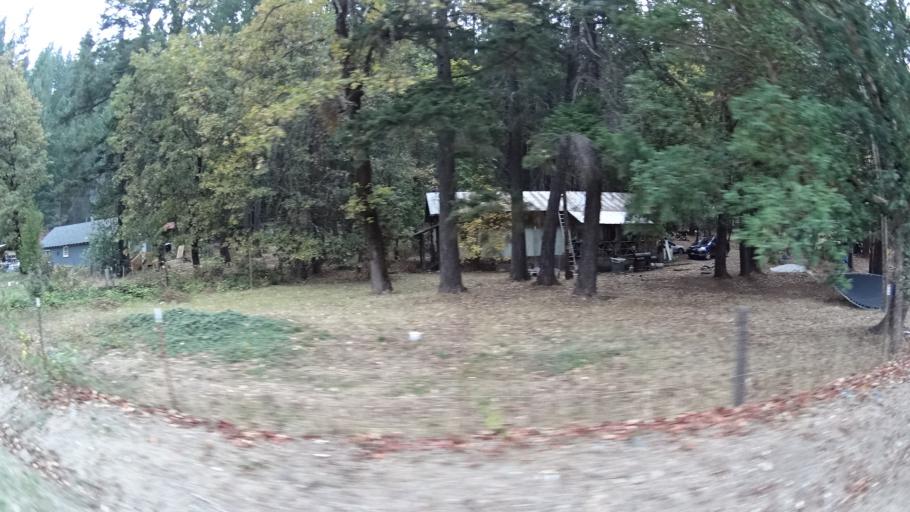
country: US
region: California
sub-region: Siskiyou County
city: Happy Camp
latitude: 41.8694
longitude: -123.4049
